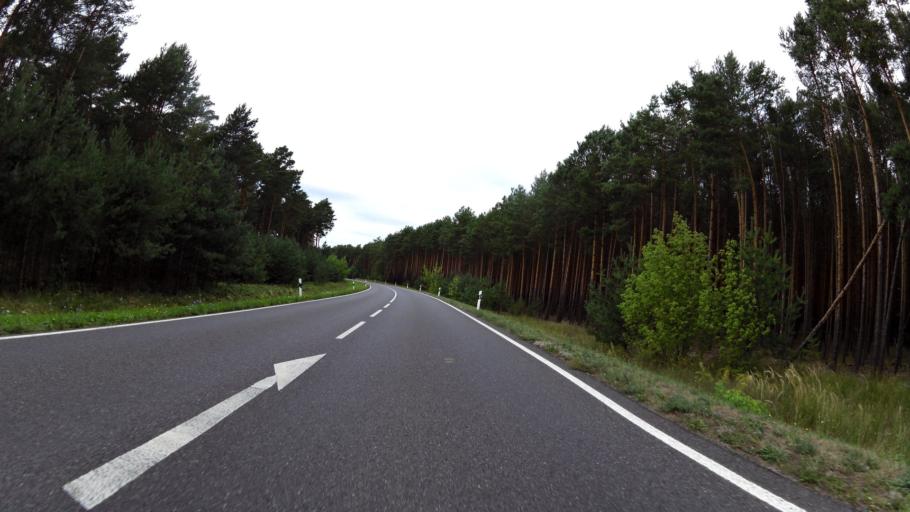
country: DE
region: Brandenburg
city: Schenkendobern
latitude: 51.8980
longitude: 14.6082
